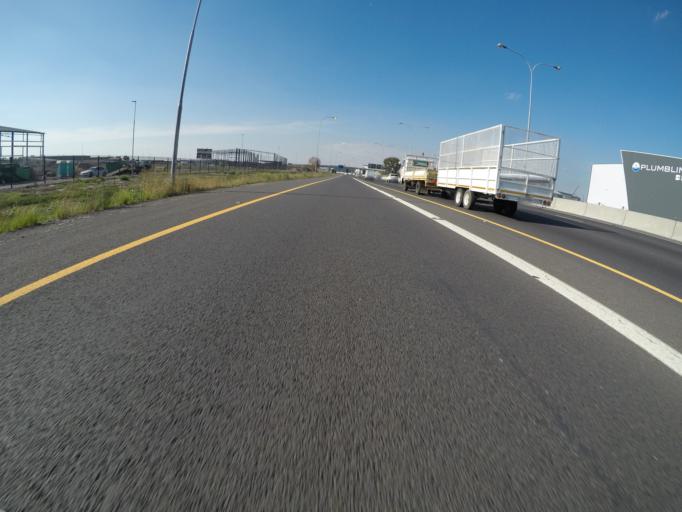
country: ZA
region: Western Cape
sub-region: City of Cape Town
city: Kraaifontein
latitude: -33.9025
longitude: 18.6752
